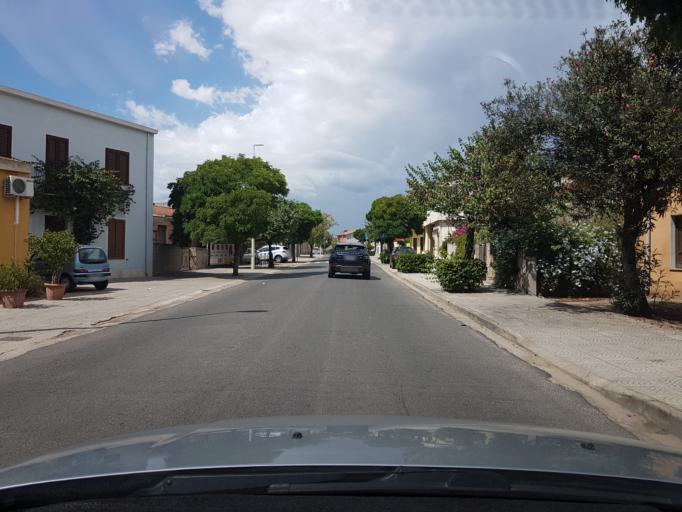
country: IT
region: Sardinia
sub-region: Provincia di Oristano
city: Riola Sardo
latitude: 39.9914
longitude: 8.5418
